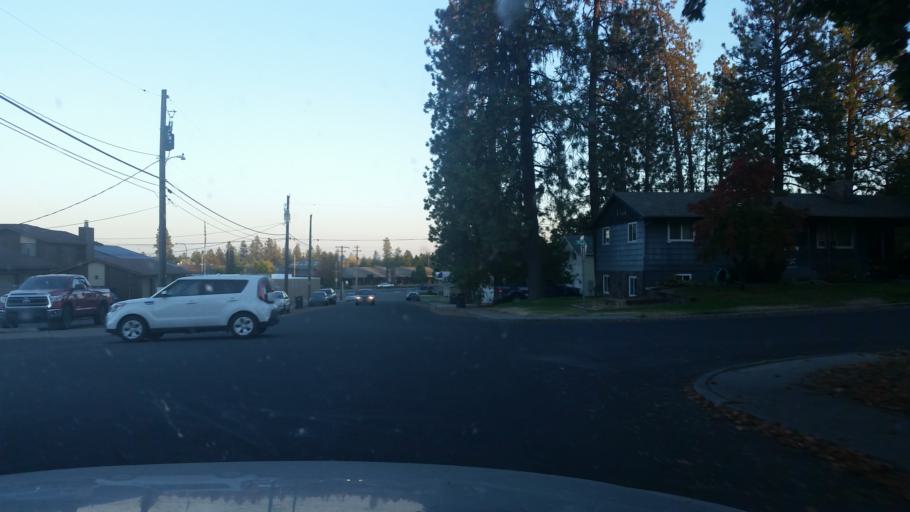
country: US
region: Washington
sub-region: Spokane County
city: Cheney
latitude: 47.4994
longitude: -117.5671
